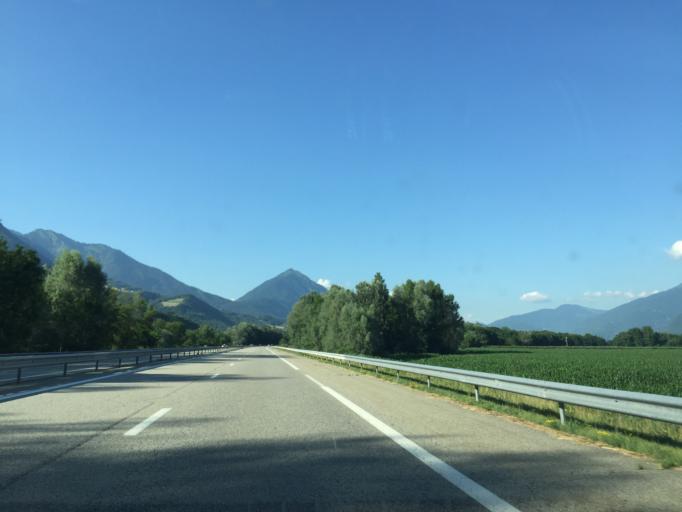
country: FR
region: Rhone-Alpes
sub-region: Departement de la Savoie
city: Gresy-sur-Isere
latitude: 45.5974
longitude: 6.2789
